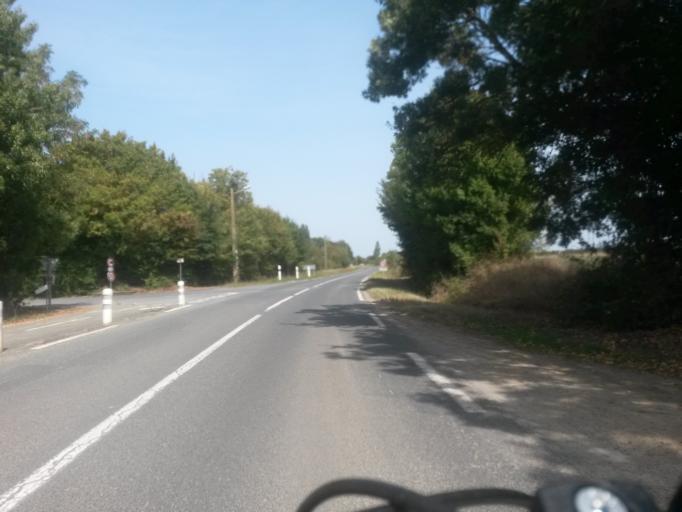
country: FR
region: Poitou-Charentes
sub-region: Departement de la Charente-Maritime
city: Saint-Xandre
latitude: 46.2134
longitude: -1.0941
